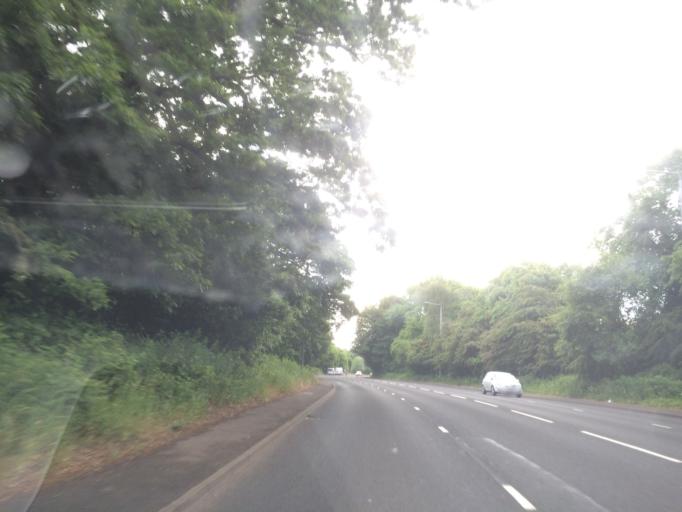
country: GB
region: Scotland
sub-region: East Renfrewshire
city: Giffnock
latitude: 55.8371
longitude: -4.3033
